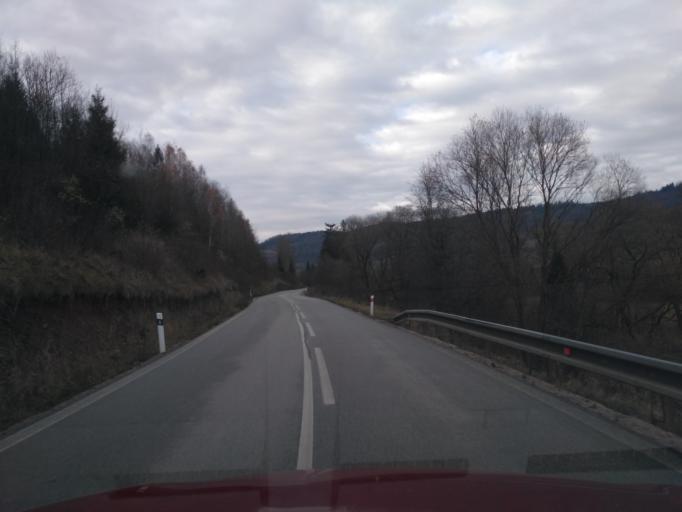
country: SK
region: Kosicky
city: Spisska Nova Ves
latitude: 48.8255
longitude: 20.6553
